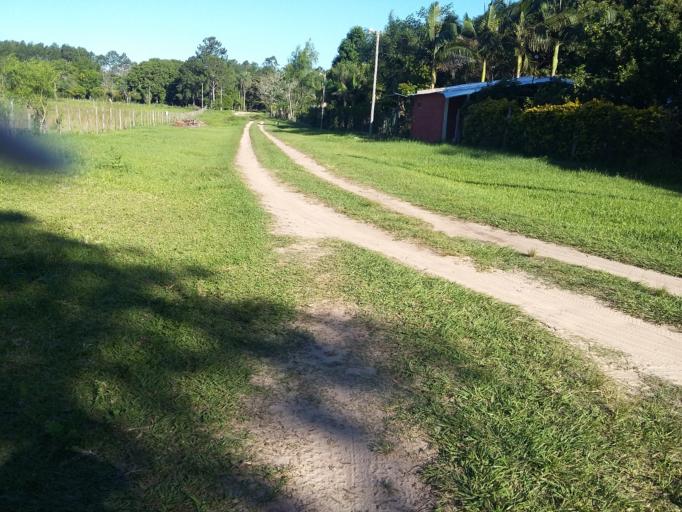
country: AR
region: Corrientes
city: San Luis del Palmar
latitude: -27.4548
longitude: -58.6501
